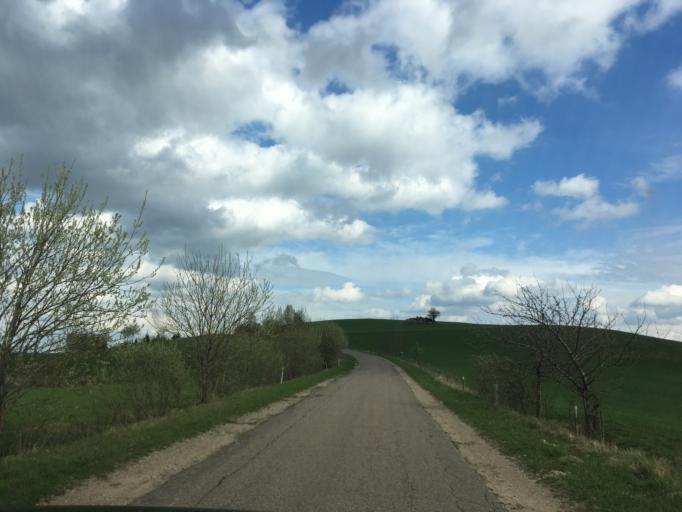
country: PL
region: Podlasie
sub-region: Suwalki
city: Suwalki
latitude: 54.3701
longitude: 22.8881
